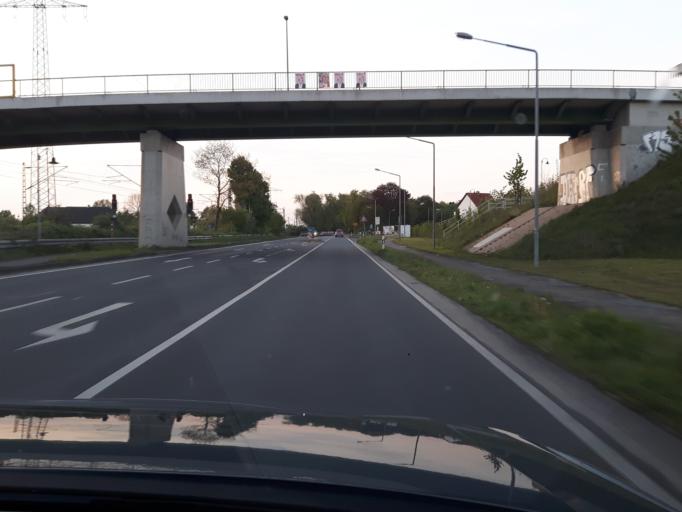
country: DE
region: North Rhine-Westphalia
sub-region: Regierungsbezirk Dusseldorf
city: Ratingen
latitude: 51.3272
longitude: 6.8290
